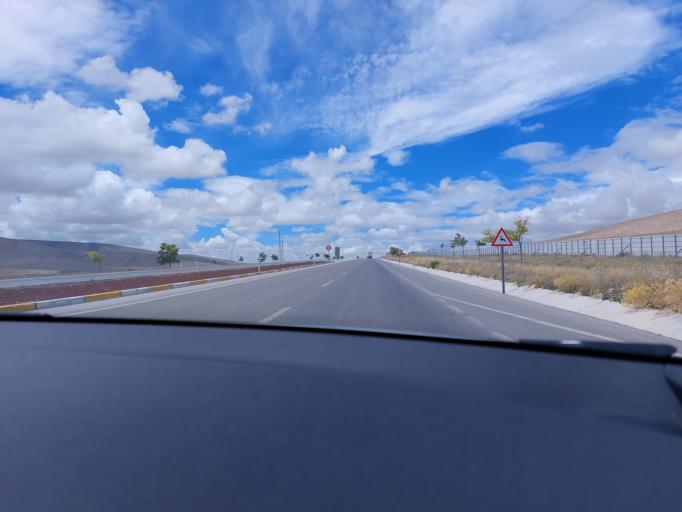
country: TR
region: Konya
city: Obruk
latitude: 38.0613
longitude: 33.0425
